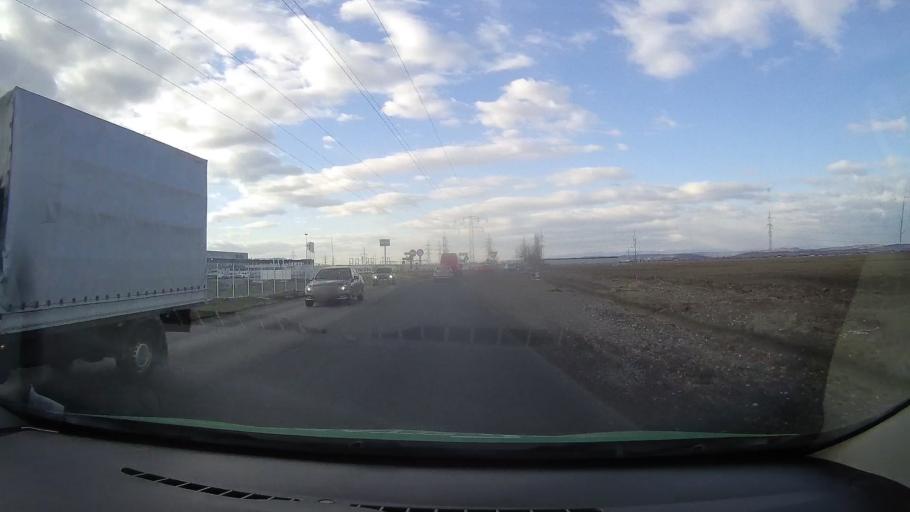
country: RO
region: Dambovita
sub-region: Comuna Comisani
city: Lazuri
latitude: 44.8748
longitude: 25.5202
